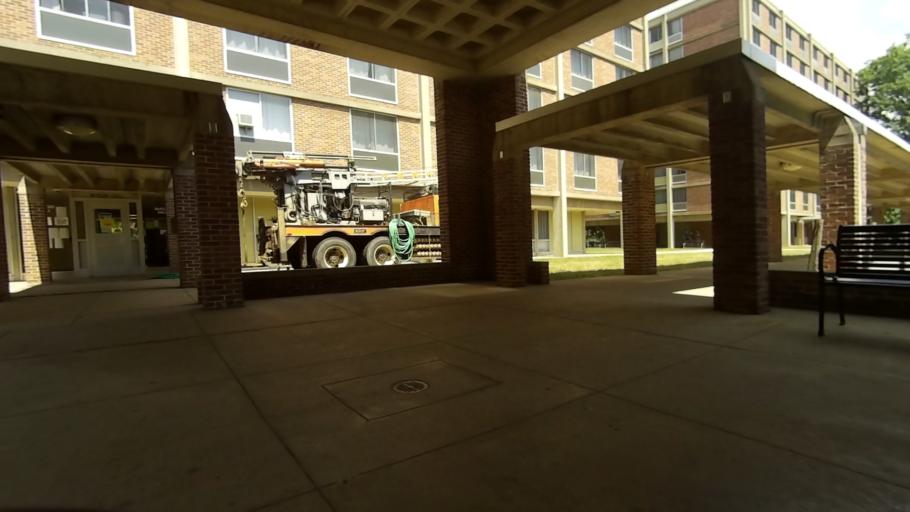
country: US
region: Pennsylvania
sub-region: Centre County
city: State College
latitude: 40.8063
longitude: -77.8613
